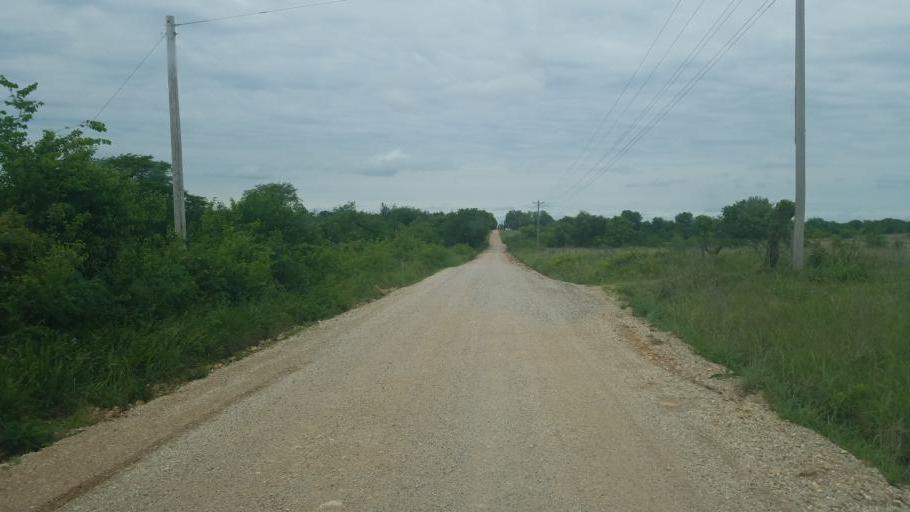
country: US
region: Missouri
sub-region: Morgan County
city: Versailles
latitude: 38.5021
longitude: -92.7898
